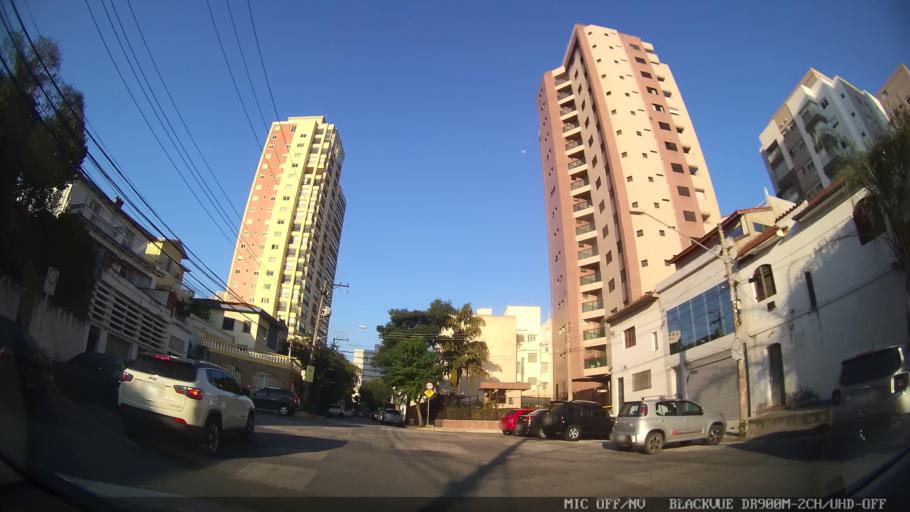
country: BR
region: Sao Paulo
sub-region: Sao Paulo
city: Sao Paulo
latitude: -23.4993
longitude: -46.6302
